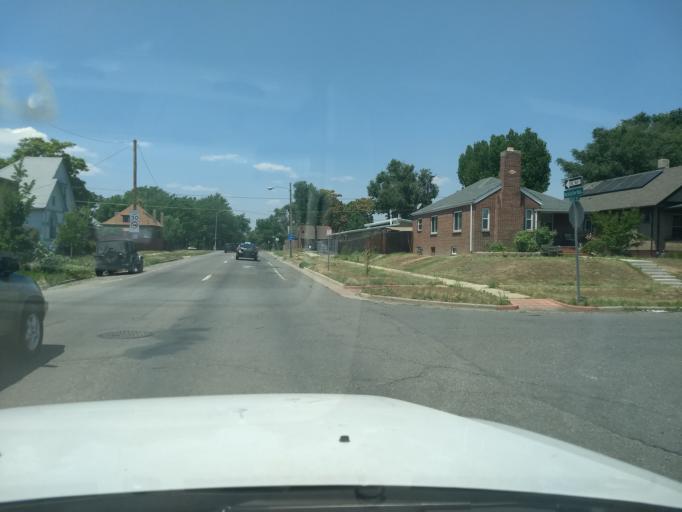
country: US
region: Colorado
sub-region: Denver County
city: Denver
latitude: 39.7620
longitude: -104.9634
